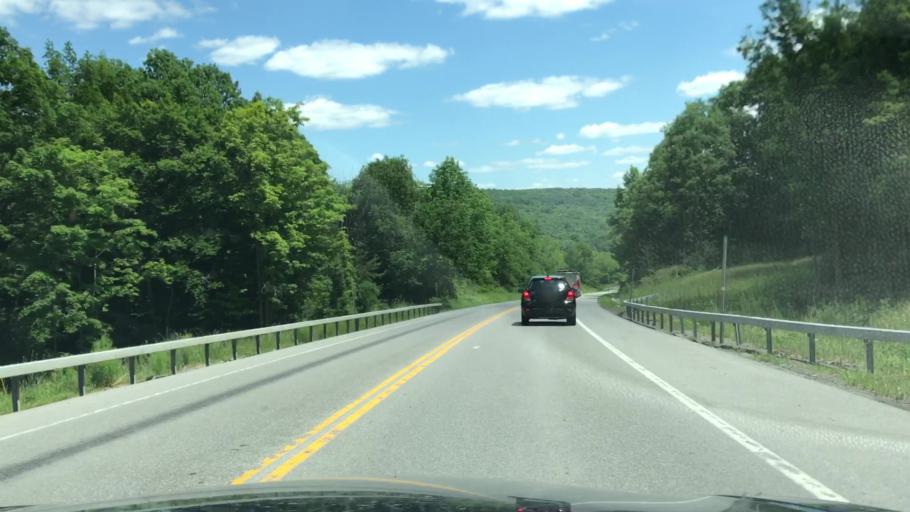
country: US
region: New York
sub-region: Wyoming County
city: Attica
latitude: 42.7698
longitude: -78.3234
